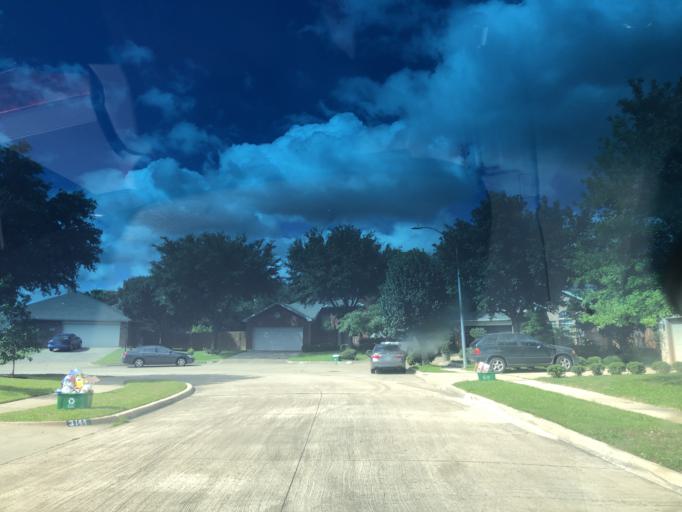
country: US
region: Texas
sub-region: Dallas County
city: Grand Prairie
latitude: 32.6939
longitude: -97.0317
